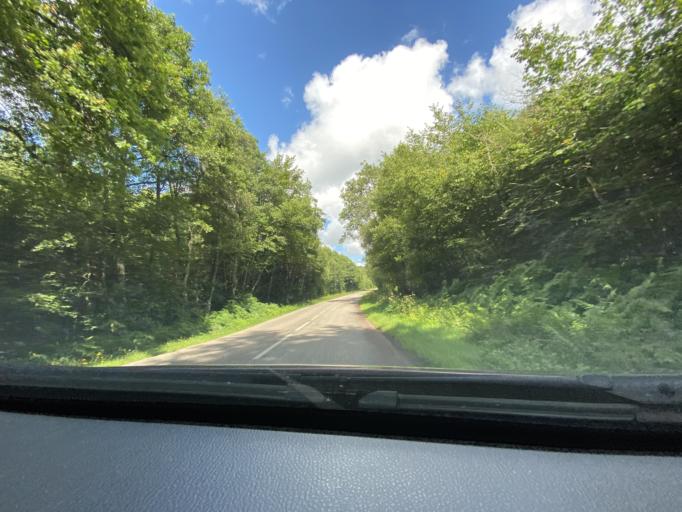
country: FR
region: Bourgogne
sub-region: Departement de la Cote-d'Or
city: Saulieu
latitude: 47.2584
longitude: 4.1132
